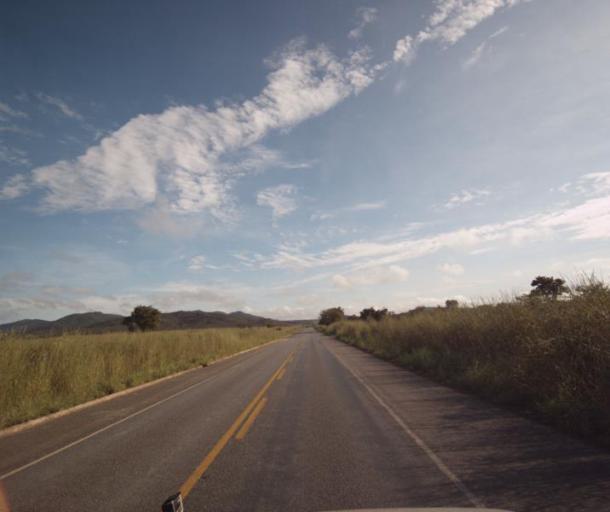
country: BR
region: Goias
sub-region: Pirenopolis
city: Pirenopolis
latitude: -15.5663
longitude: -48.6217
